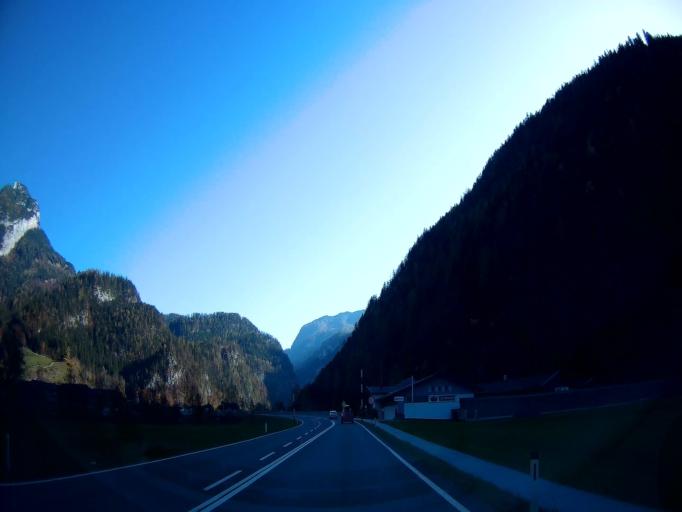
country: AT
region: Salzburg
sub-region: Politischer Bezirk Zell am See
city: Sankt Martin bei Lofer
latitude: 47.5235
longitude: 12.7469
